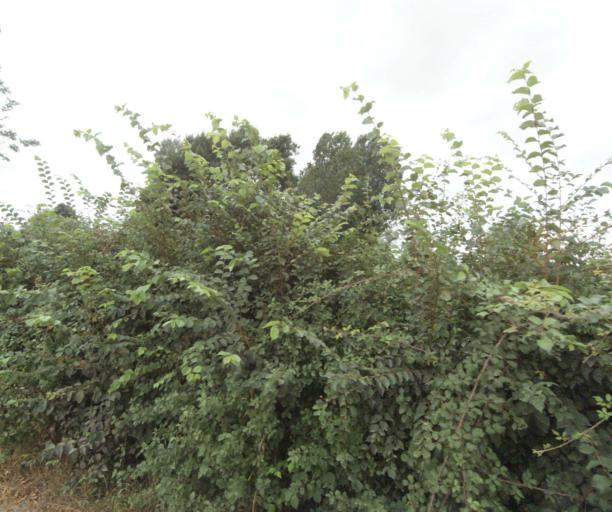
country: FR
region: Nord-Pas-de-Calais
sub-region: Departement du Nord
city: Linselles
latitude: 50.7329
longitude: 3.1021
